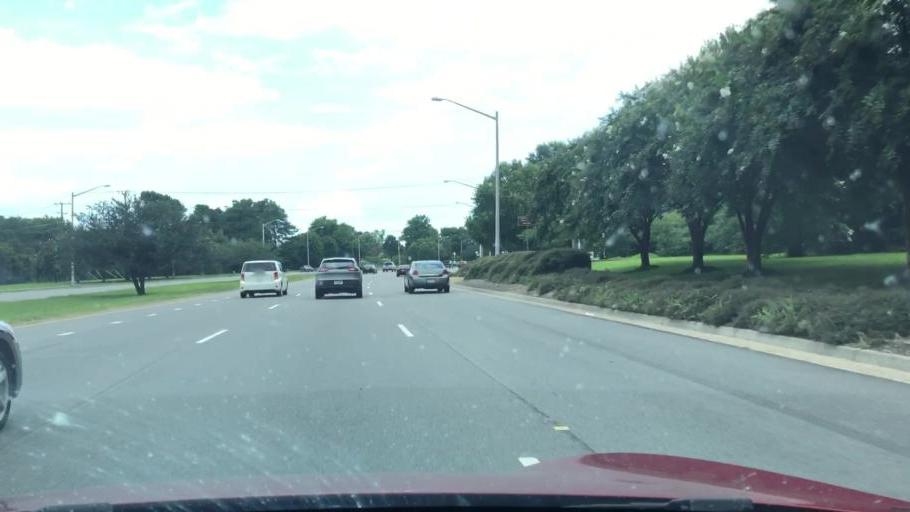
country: US
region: Virginia
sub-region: City of Chesapeake
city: Chesapeake
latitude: 36.8504
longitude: -76.1365
